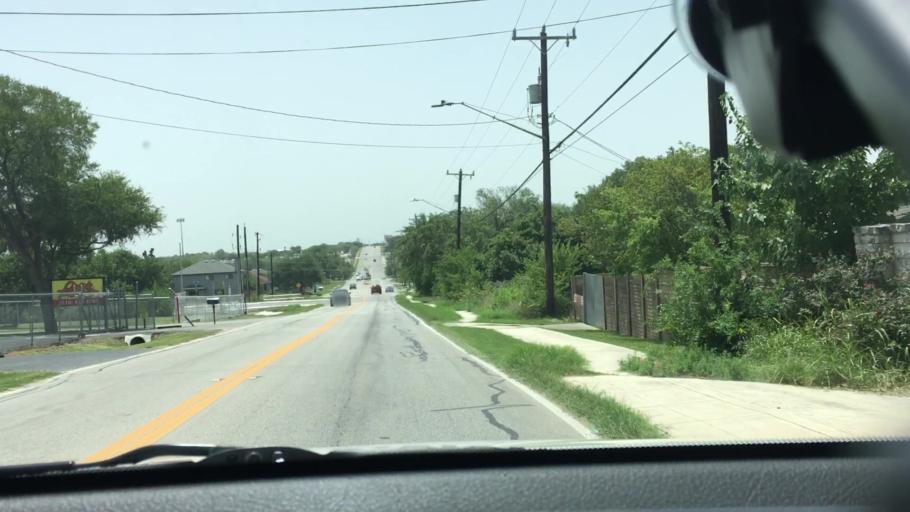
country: US
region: Texas
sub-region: Bexar County
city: Live Oak
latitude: 29.5731
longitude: -98.3586
